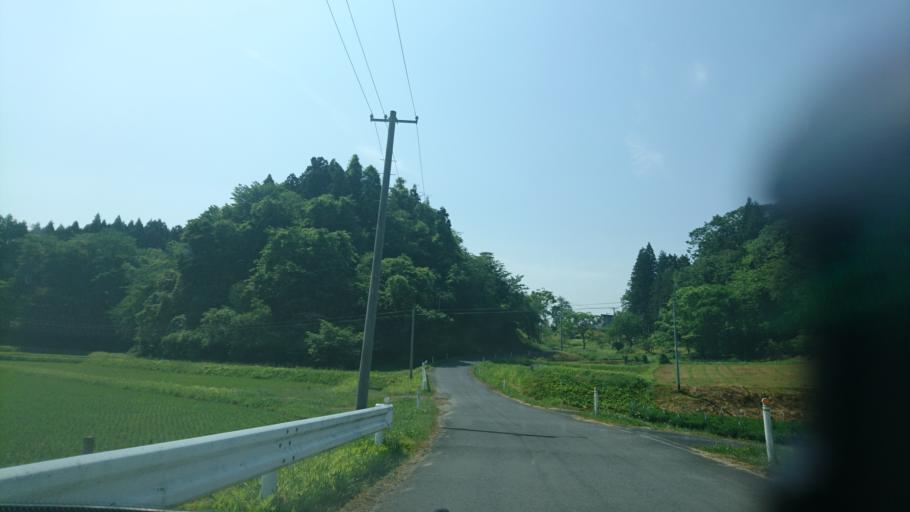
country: JP
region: Iwate
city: Ichinoseki
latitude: 38.8958
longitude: 141.3362
